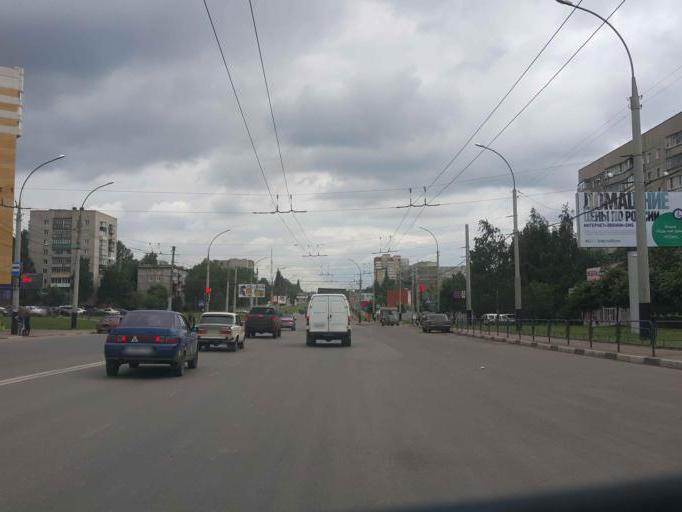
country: RU
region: Tambov
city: Tambov
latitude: 52.7602
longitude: 41.4026
